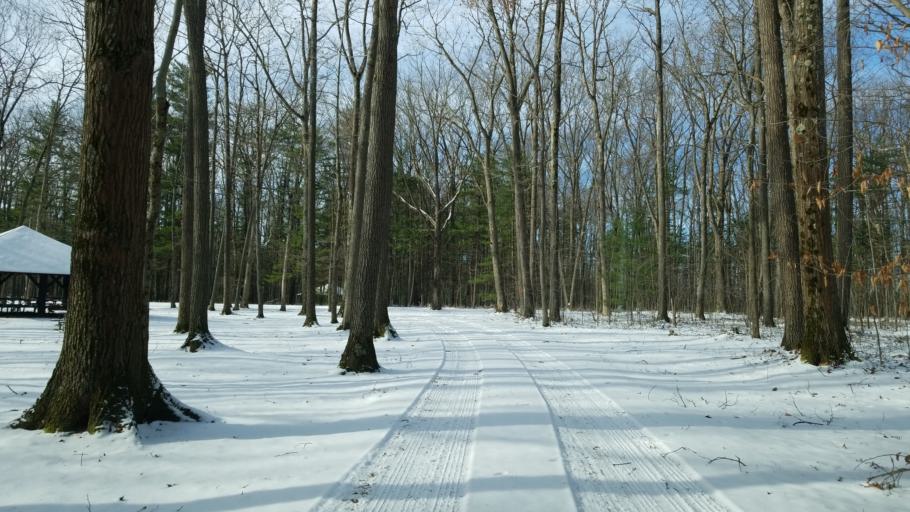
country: US
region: Pennsylvania
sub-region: Clearfield County
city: Clearfield
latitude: 41.1140
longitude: -78.5242
